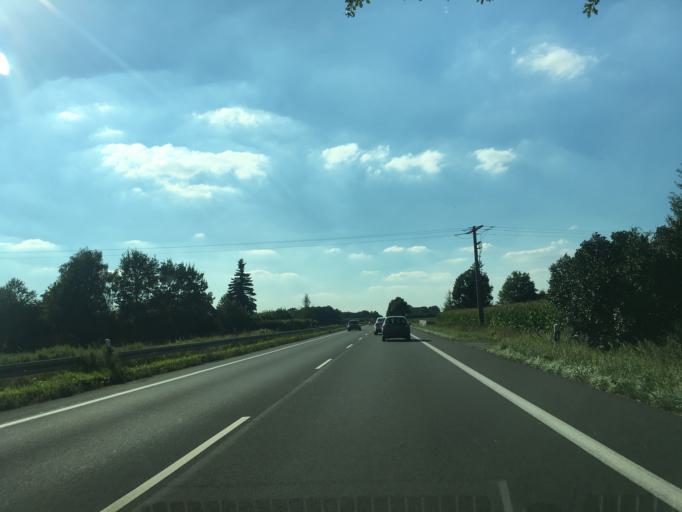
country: DE
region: North Rhine-Westphalia
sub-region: Regierungsbezirk Munster
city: Sassenberg
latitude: 51.9444
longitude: 8.0517
